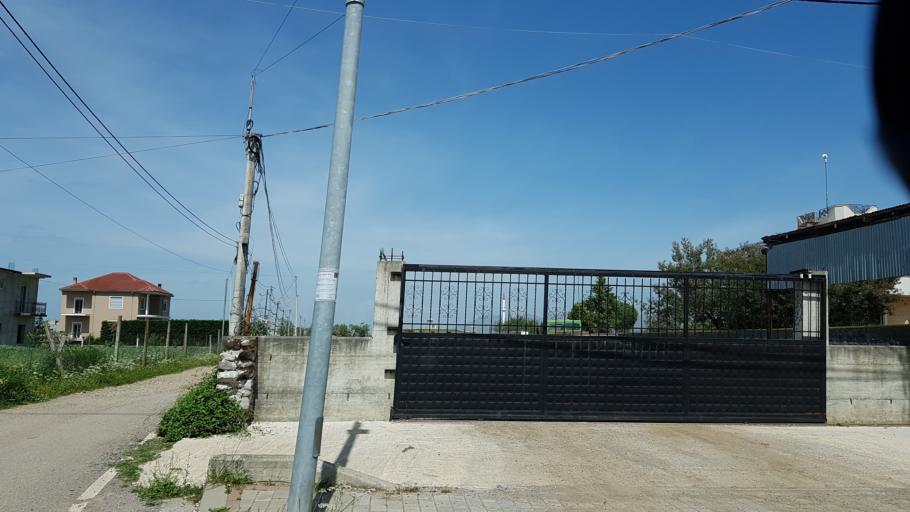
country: AL
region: Shkoder
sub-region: Rrethi i Shkodres
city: Guri i Zi
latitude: 42.1092
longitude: 19.5651
